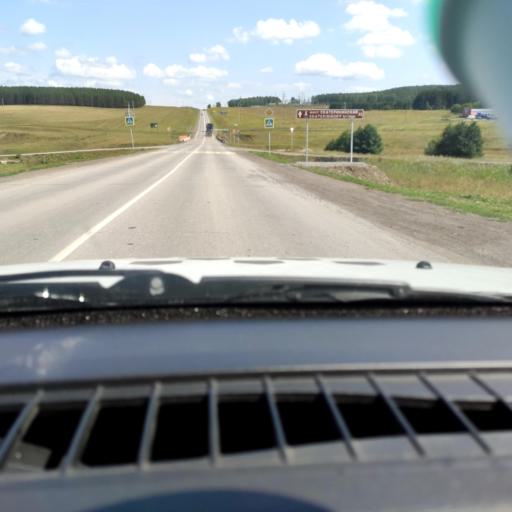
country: RU
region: Bashkortostan
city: Verkhniye Kigi
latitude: 55.3981
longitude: 58.6086
